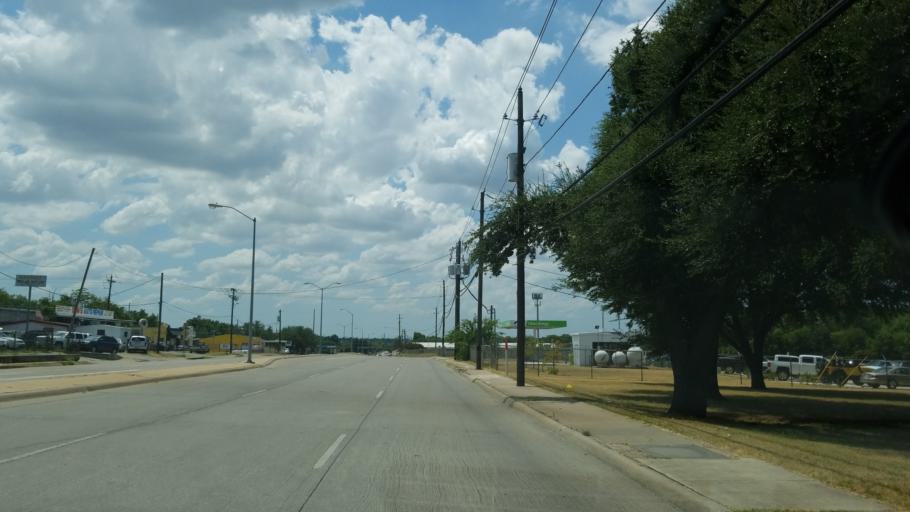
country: US
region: Texas
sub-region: Dallas County
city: Cockrell Hill
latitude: 32.7244
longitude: -96.8917
